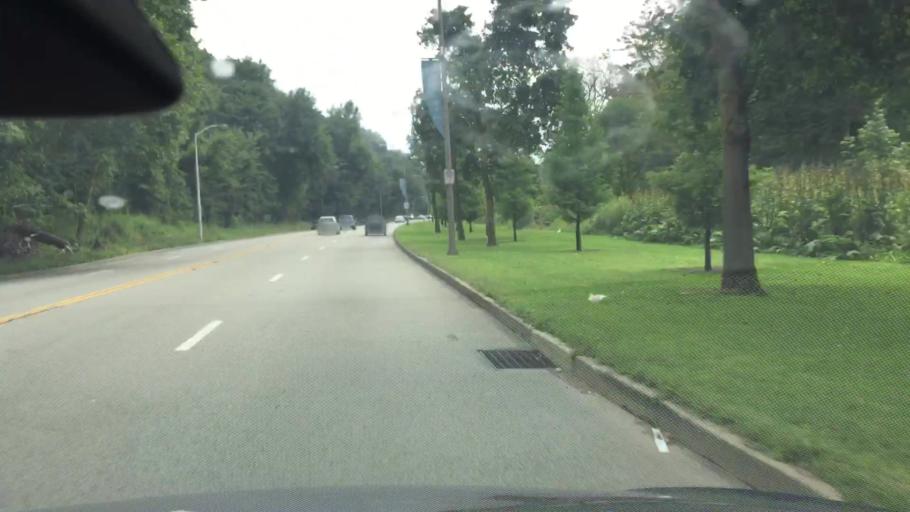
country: US
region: Pennsylvania
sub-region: Allegheny County
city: Aspinwall
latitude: 40.4811
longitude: -79.9080
